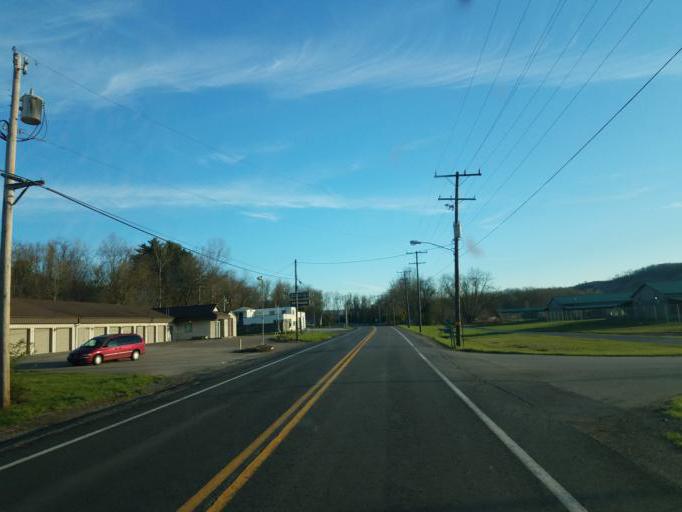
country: US
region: Ohio
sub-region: Jefferson County
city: Brilliant
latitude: 40.2374
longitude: -80.6512
